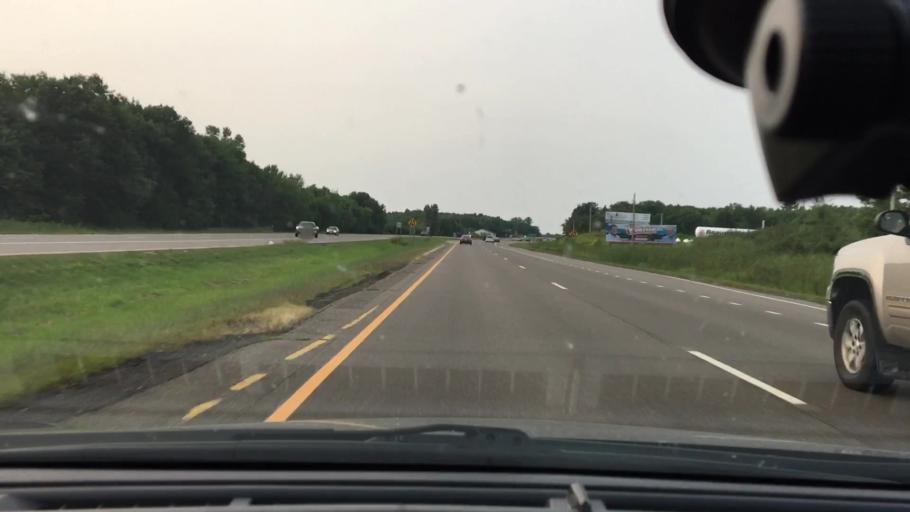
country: US
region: Minnesota
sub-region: Mille Lacs County
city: Vineland
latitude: 46.0952
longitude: -93.6440
